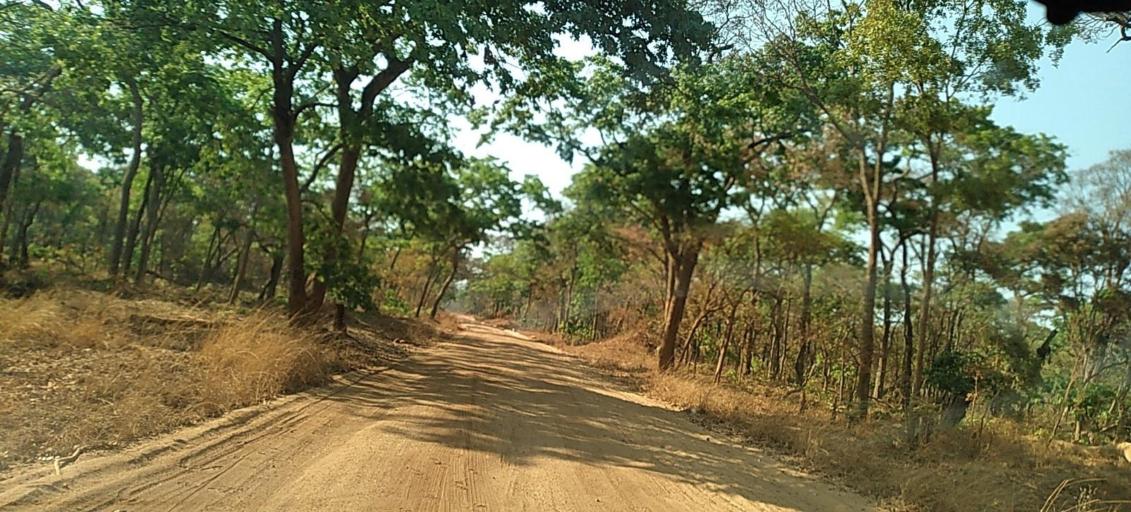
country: ZM
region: North-Western
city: Kasempa
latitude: -13.6690
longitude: 26.0146
